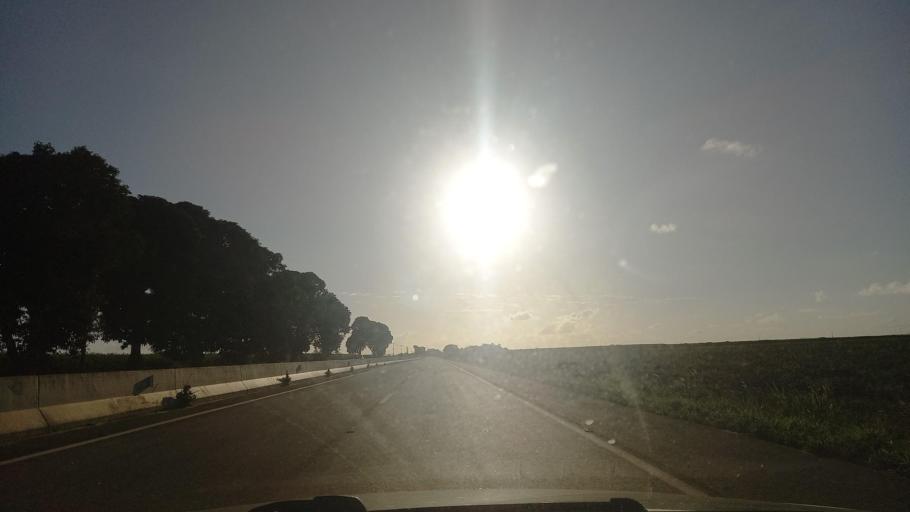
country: BR
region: Alagoas
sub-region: Campo Alegre
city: Campo Alegre
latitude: -9.7941
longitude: -36.3105
